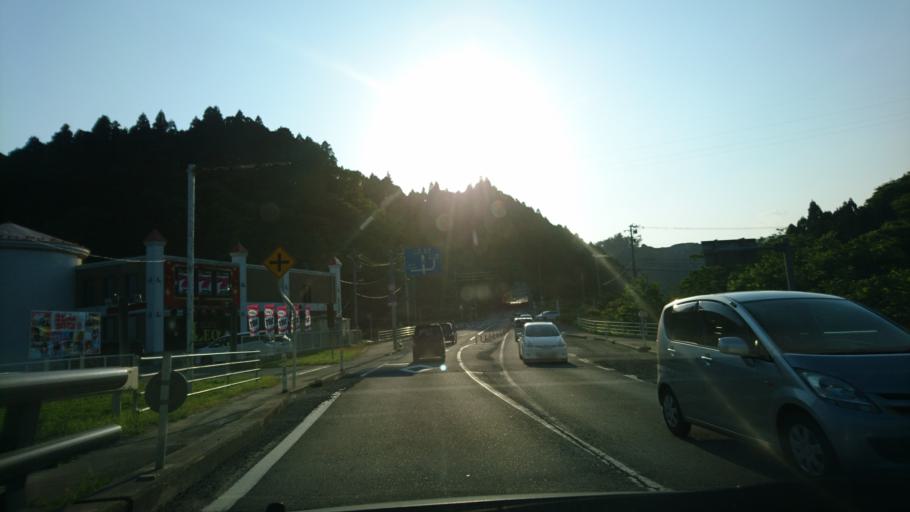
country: JP
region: Iwate
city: Ofunato
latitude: 38.9122
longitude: 141.5321
